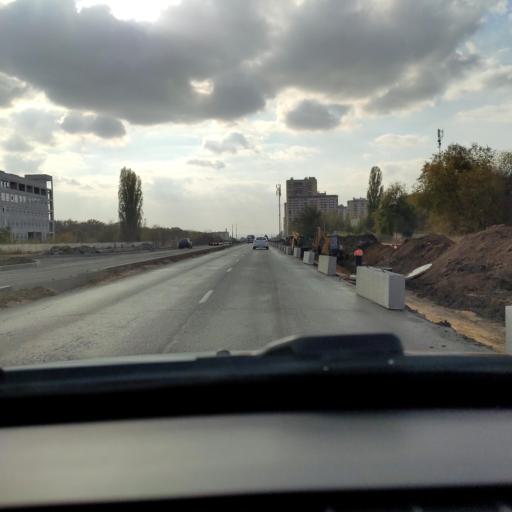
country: RU
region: Voronezj
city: Shilovo
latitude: 51.5700
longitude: 39.1334
